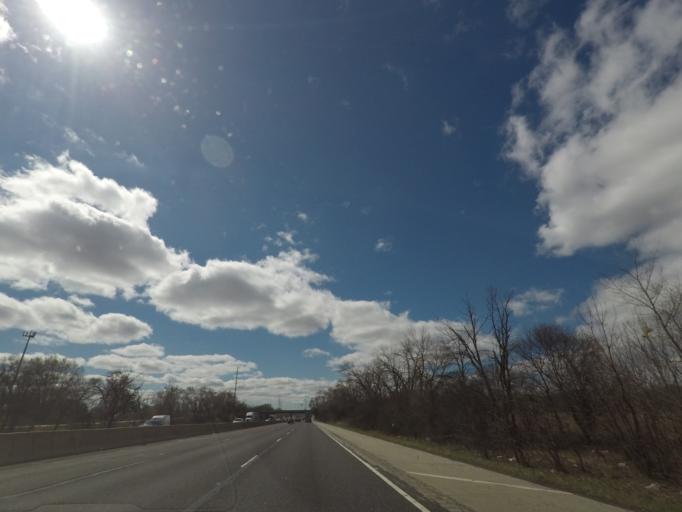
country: US
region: Illinois
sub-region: Will County
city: Crystal Lawns
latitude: 41.5970
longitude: -88.1632
